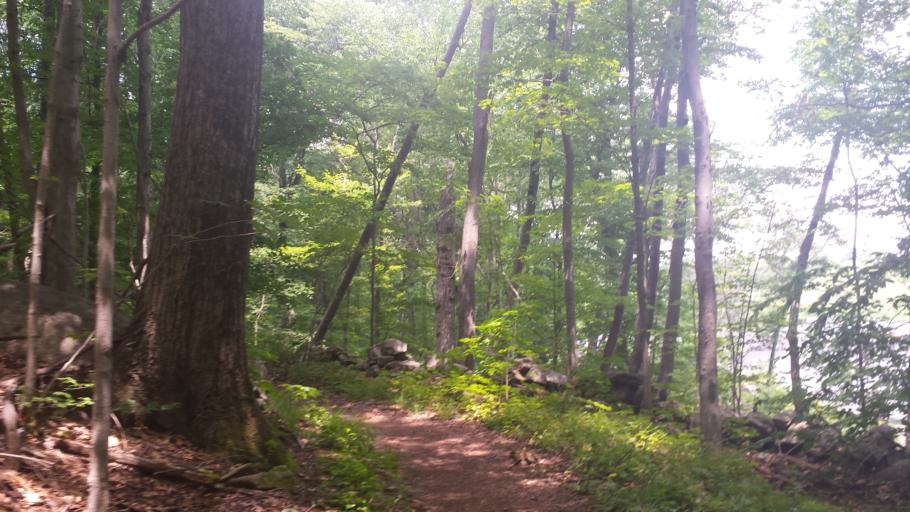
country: US
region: New York
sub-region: Westchester County
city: Scarsdale
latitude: 40.9872
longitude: -73.7491
